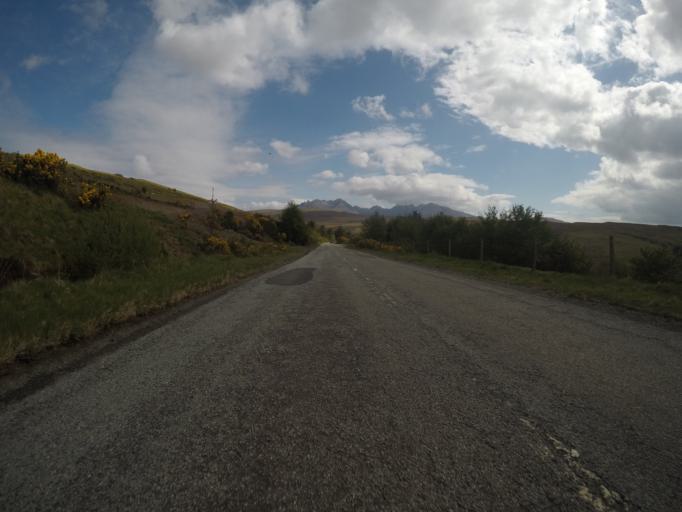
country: GB
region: Scotland
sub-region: Highland
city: Isle of Skye
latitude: 57.3022
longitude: -6.2982
